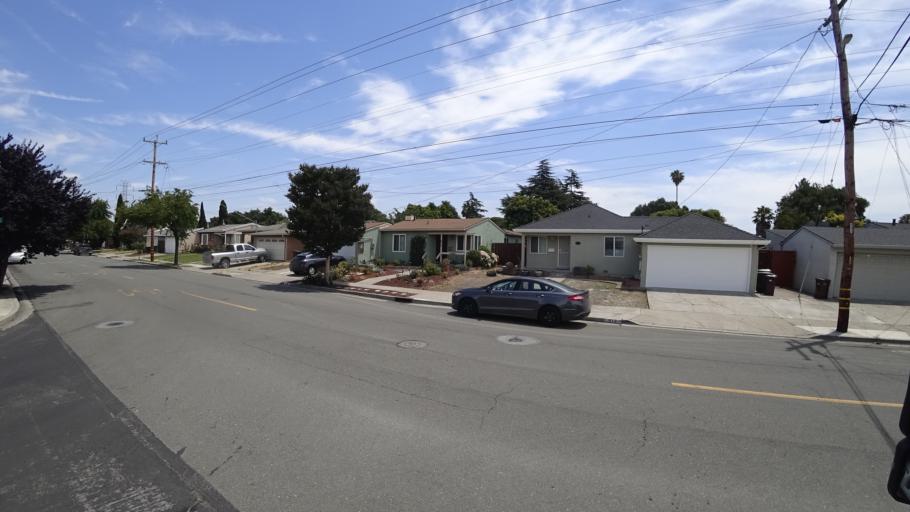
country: US
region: California
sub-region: Alameda County
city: Hayward
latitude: 37.6438
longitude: -122.0895
